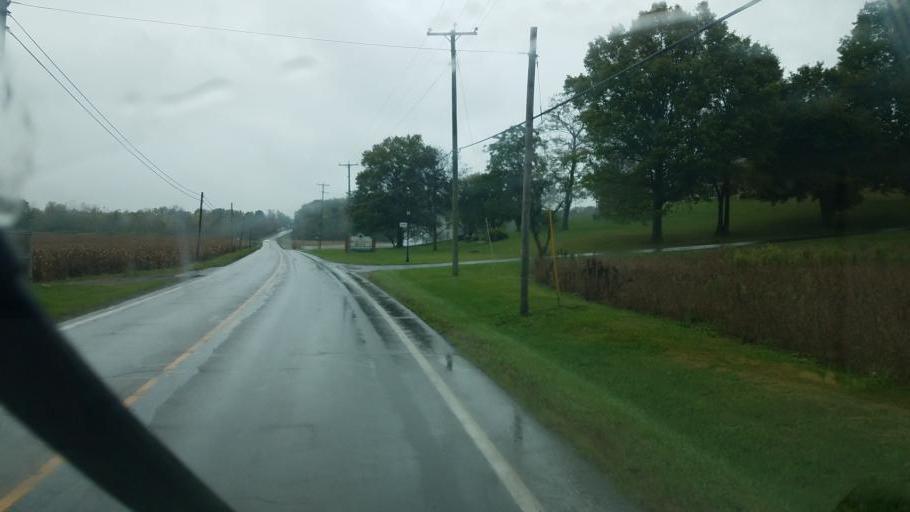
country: US
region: Ohio
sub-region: Holmes County
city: Millersburg
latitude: 40.6113
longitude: -81.9146
